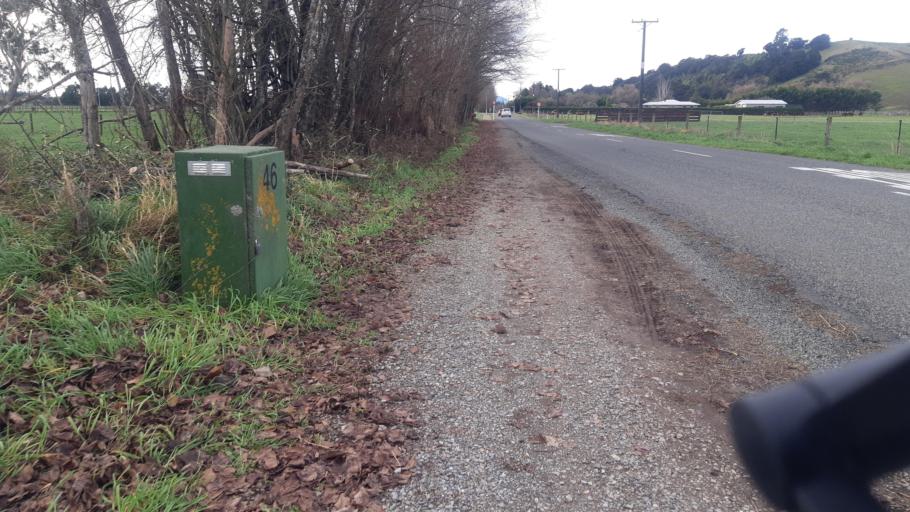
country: NZ
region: Tasman
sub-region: Tasman District
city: Wakefield
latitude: -41.3954
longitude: 173.0752
